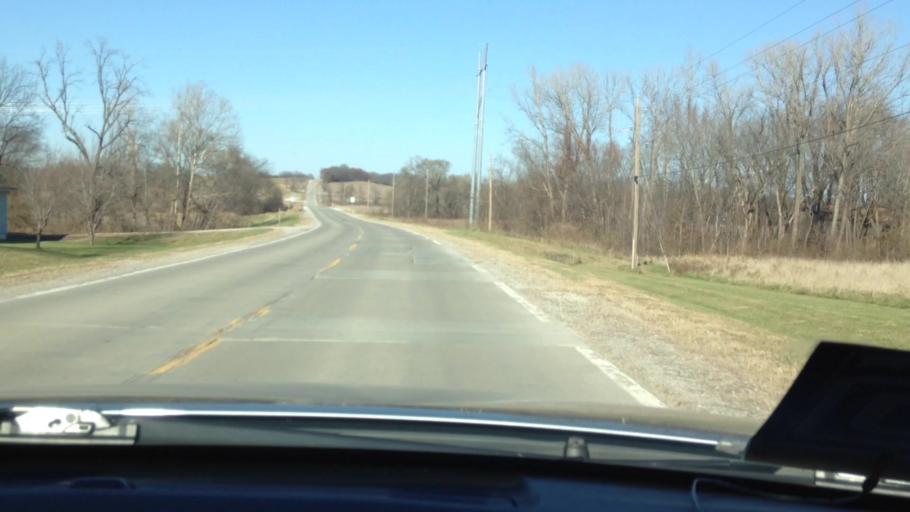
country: US
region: Missouri
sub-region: Platte County
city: Platte City
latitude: 39.5040
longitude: -94.7995
